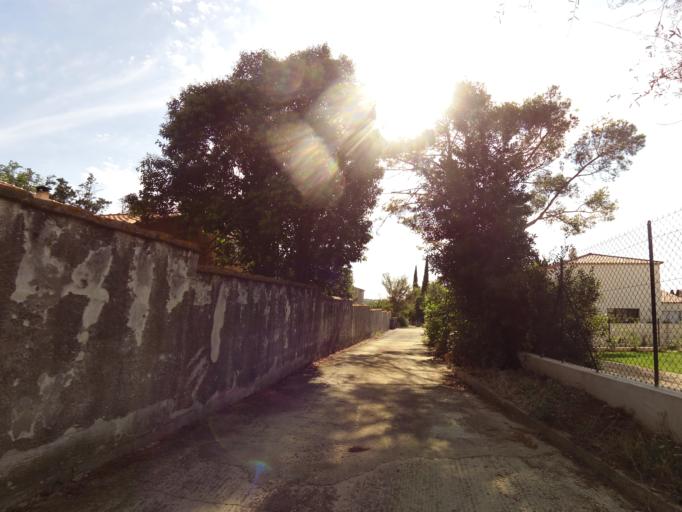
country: FR
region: Languedoc-Roussillon
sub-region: Departement du Gard
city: Gallargues-le-Montueux
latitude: 43.7217
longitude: 4.1690
